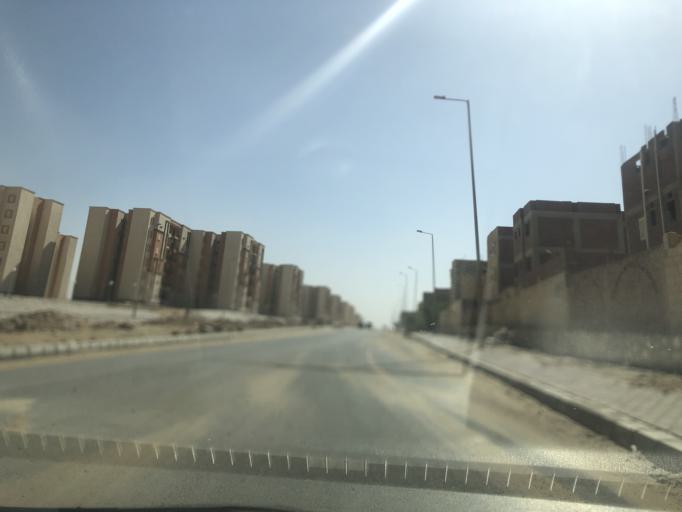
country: EG
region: Al Jizah
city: Madinat Sittah Uktubar
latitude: 29.9363
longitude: 30.9771
